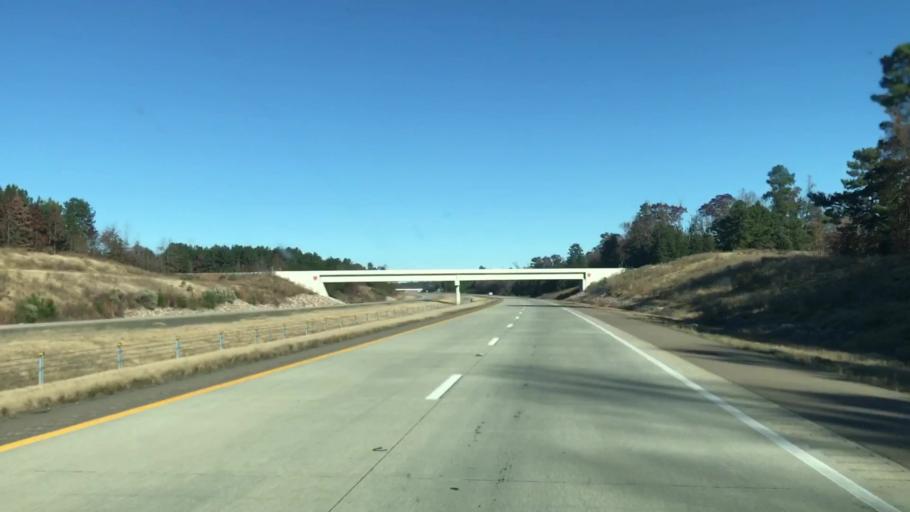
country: US
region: Louisiana
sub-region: Caddo Parish
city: Vivian
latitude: 33.0493
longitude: -93.9007
